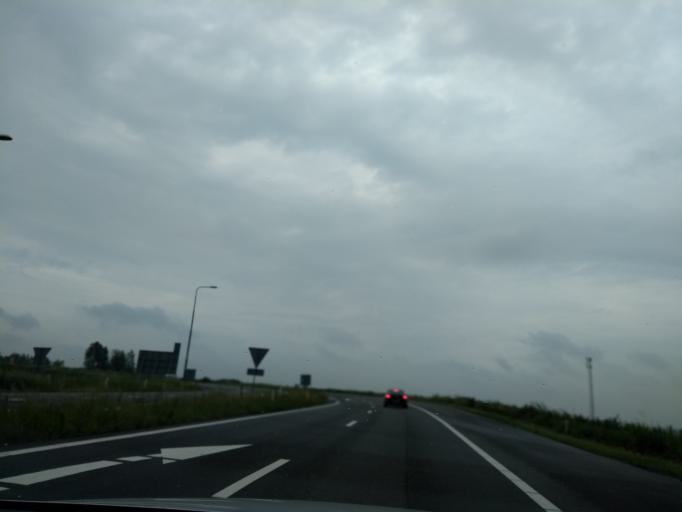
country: NL
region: Utrecht
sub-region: Gemeente Bunschoten
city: Spakenburg
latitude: 52.3142
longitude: 5.3292
